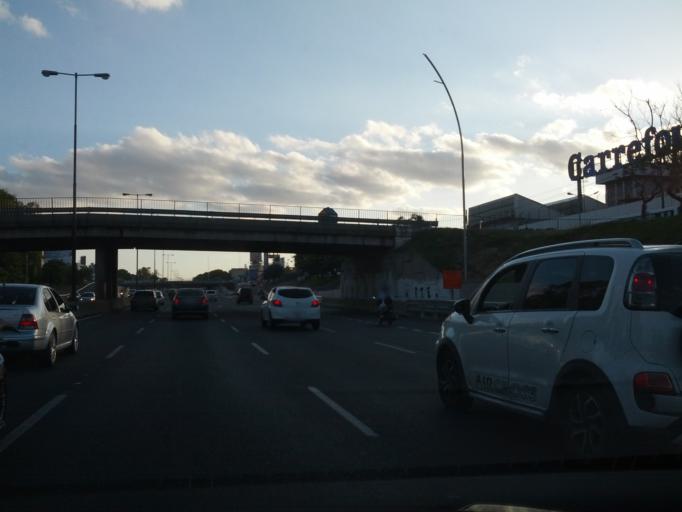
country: AR
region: Buenos Aires
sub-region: Partido de General San Martin
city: General San Martin
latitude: -34.5856
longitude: -58.5169
